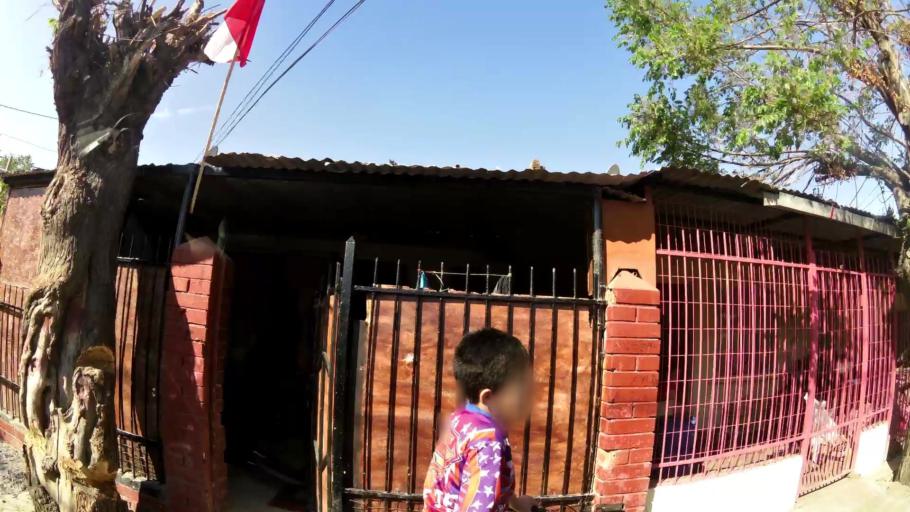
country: CL
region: Santiago Metropolitan
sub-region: Provincia de Santiago
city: La Pintana
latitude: -33.5607
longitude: -70.6175
